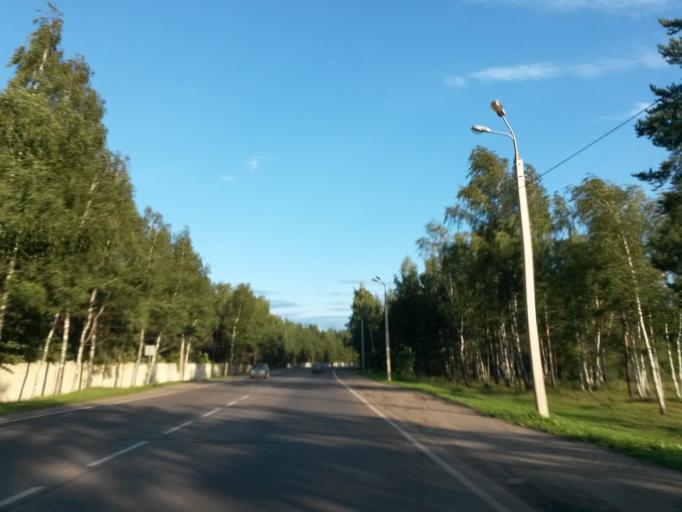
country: RU
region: Jaroslavl
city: Yaroslavl
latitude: 57.6758
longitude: 39.9050
